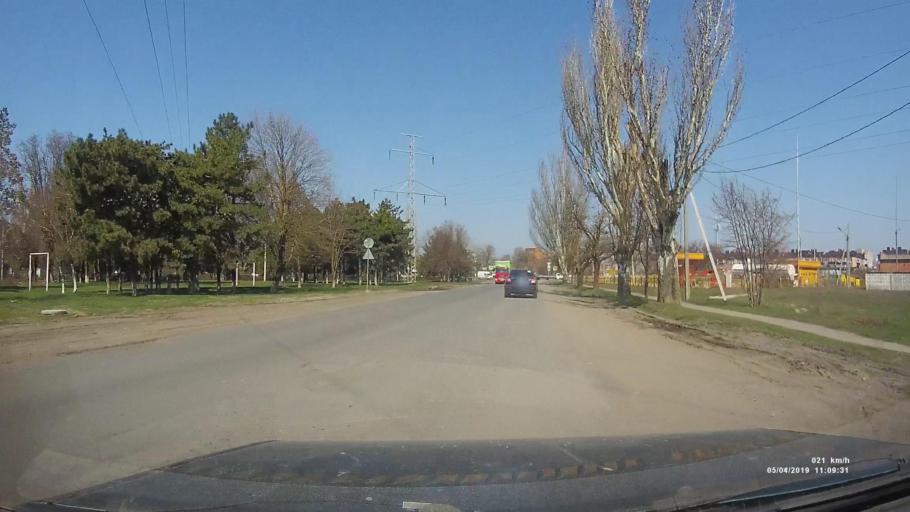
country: RU
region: Rostov
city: Azov
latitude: 47.0904
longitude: 39.4328
